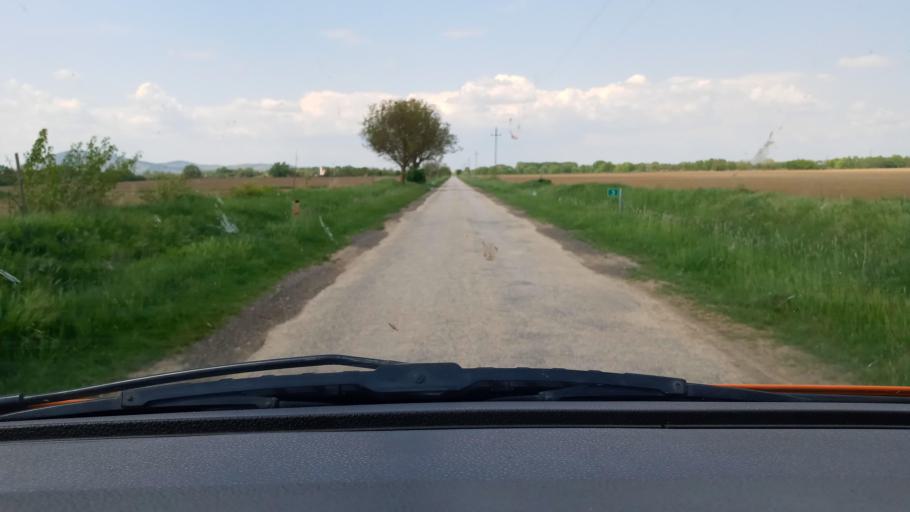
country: HU
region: Baranya
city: Beremend
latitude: 45.8097
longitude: 18.5154
